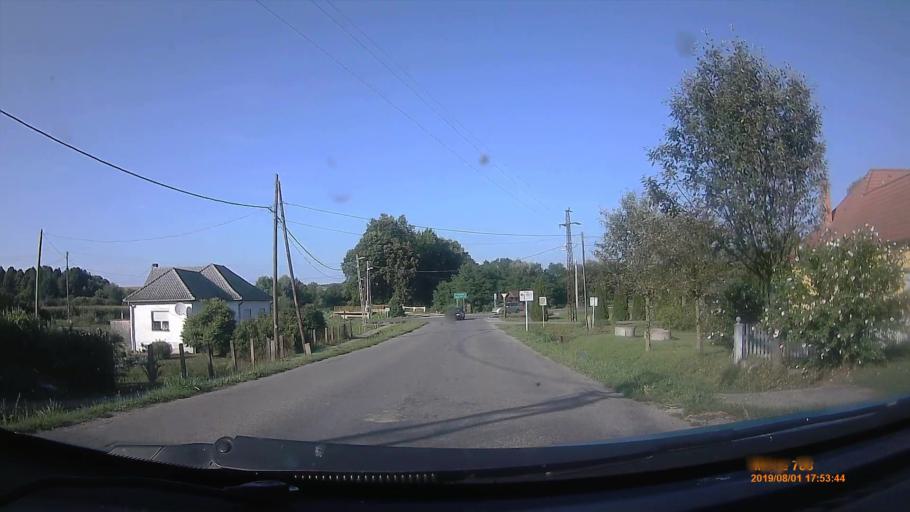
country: HU
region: Baranya
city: Sasd
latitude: 46.1909
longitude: 18.1536
